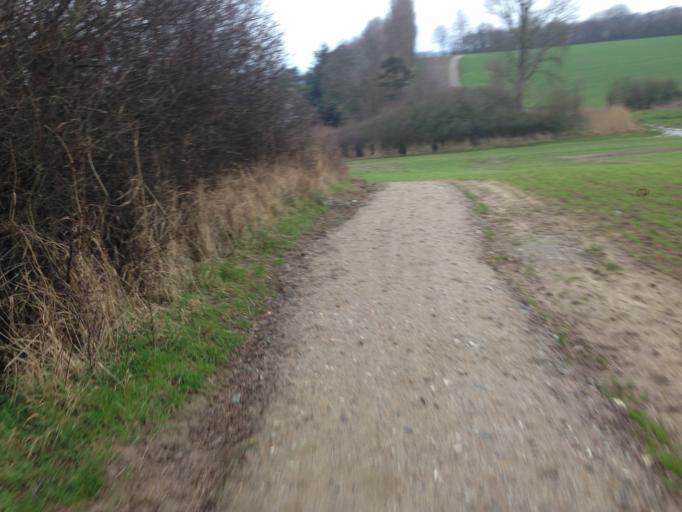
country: DK
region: South Denmark
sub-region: Sonderborg Kommune
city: Horuphav
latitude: 54.9047
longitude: 9.9137
